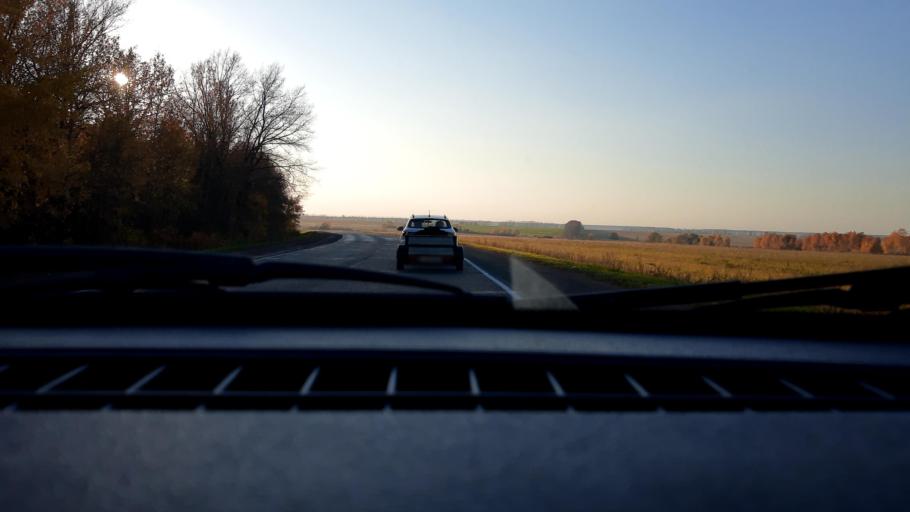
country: RU
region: Bashkortostan
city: Asanovo
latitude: 54.8267
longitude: 55.6370
